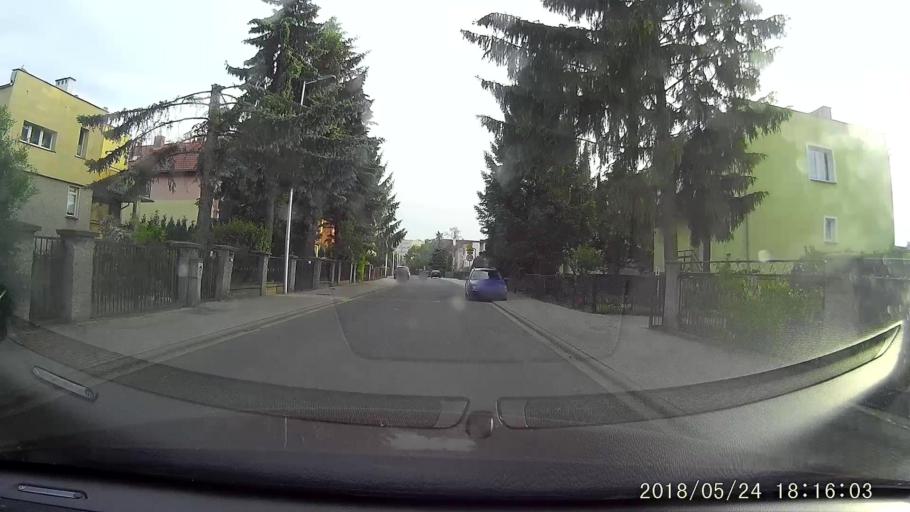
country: PL
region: Lower Silesian Voivodeship
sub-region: Powiat zgorzelecki
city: Zgorzelec
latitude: 51.1578
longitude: 15.0226
